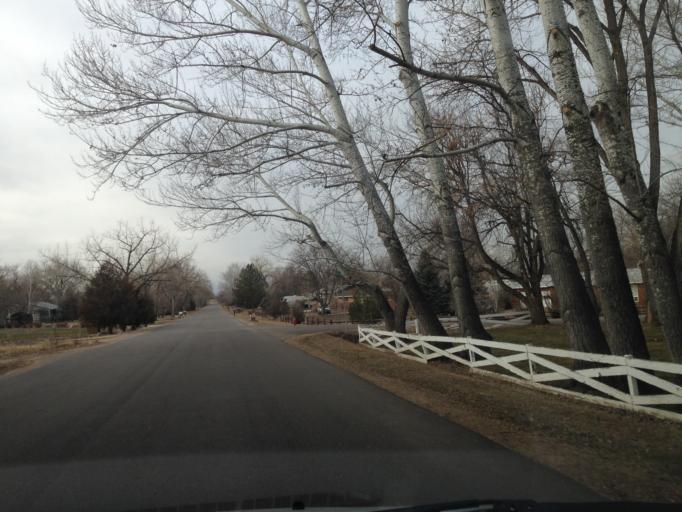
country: US
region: Colorado
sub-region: Boulder County
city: Erie
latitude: 40.0448
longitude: -105.0880
